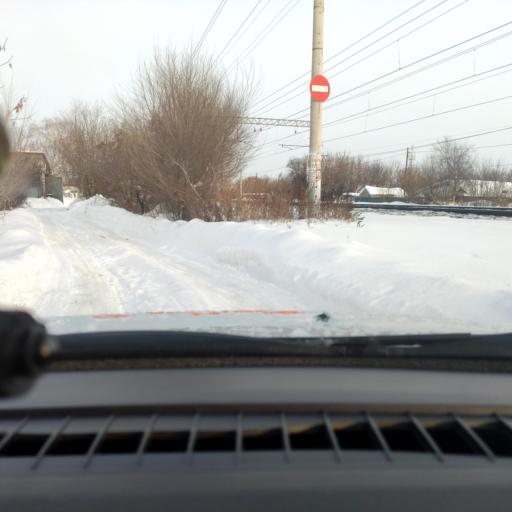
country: RU
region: Samara
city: Smyshlyayevka
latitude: 53.2437
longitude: 50.3439
